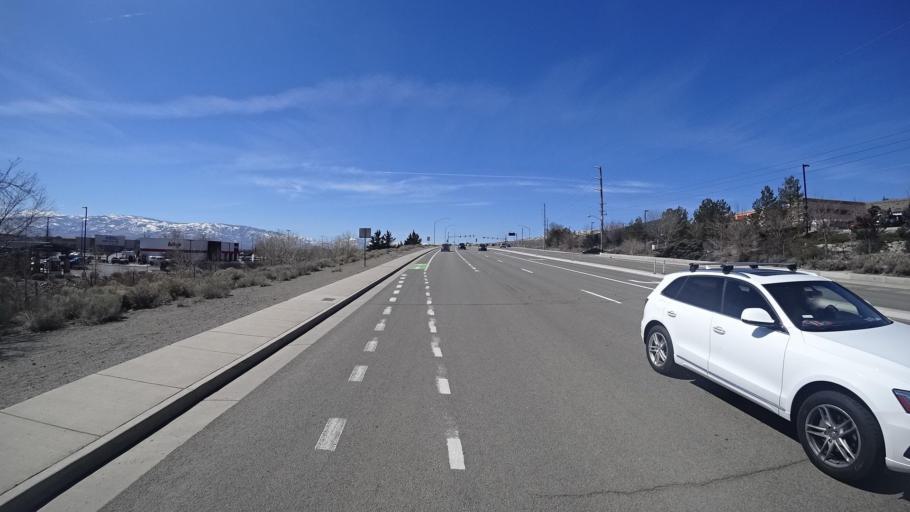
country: US
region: Nevada
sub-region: Washoe County
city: Sparks
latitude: 39.5566
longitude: -119.7834
